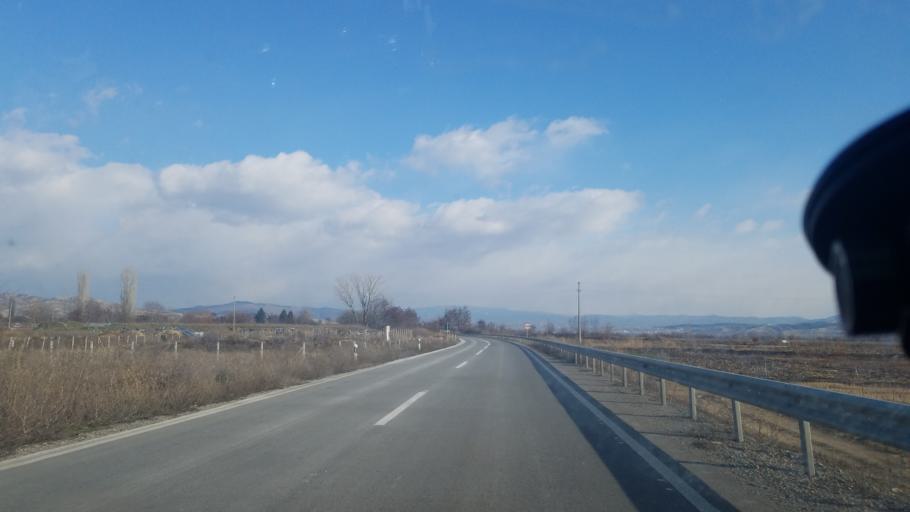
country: MK
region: Kocani
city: Kochani
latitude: 41.9017
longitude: 22.4054
